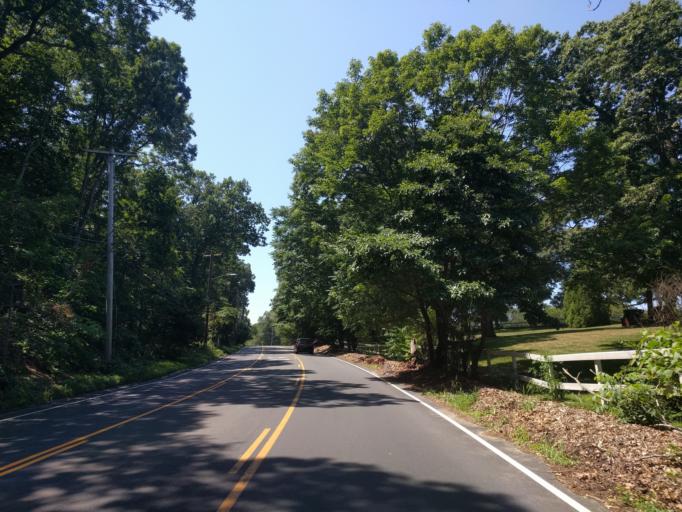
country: US
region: New York
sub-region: Suffolk County
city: Fort Salonga
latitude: 40.9046
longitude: -73.3207
